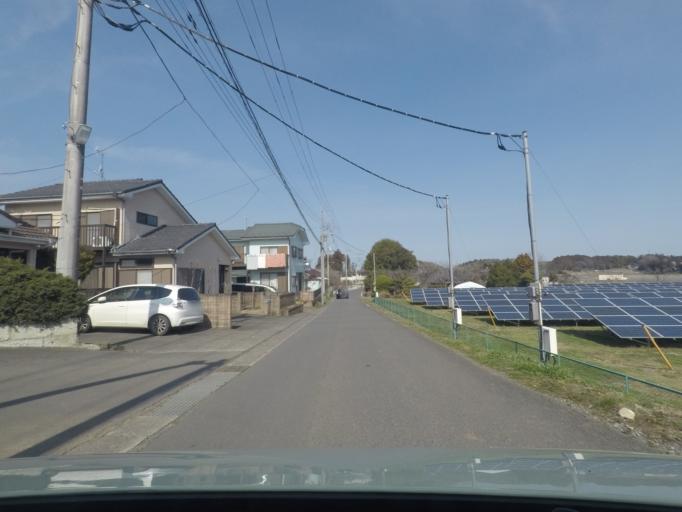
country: JP
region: Ibaraki
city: Ishioka
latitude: 36.1968
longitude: 140.3144
